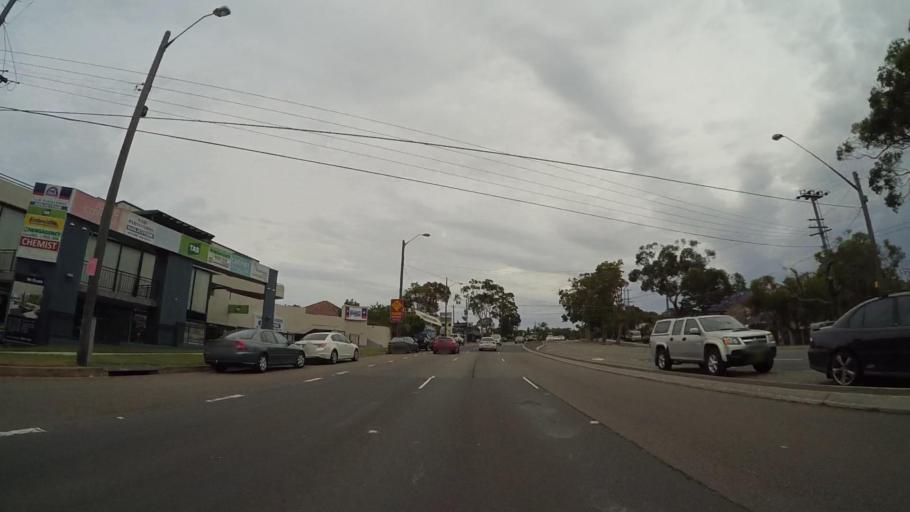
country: AU
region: New South Wales
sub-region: Sutherland Shire
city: Kareela
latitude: -34.0138
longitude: 151.0943
